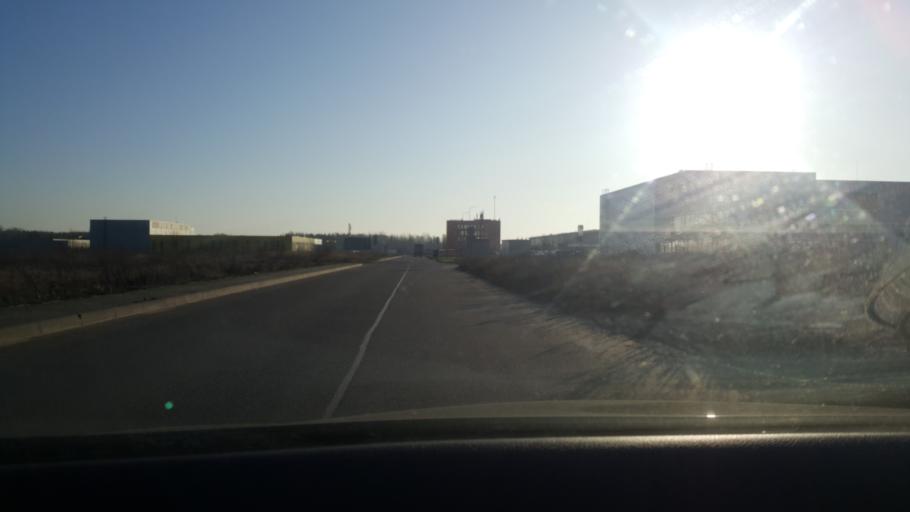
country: LT
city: Ramuciai
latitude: 54.9323
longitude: 24.0355
